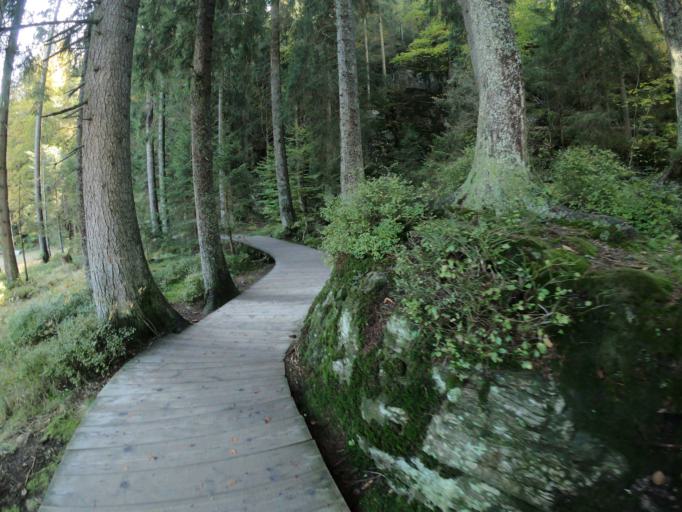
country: DE
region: Bavaria
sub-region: Lower Bavaria
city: Bayerisch Eisenstein
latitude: 49.0972
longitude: 13.1506
